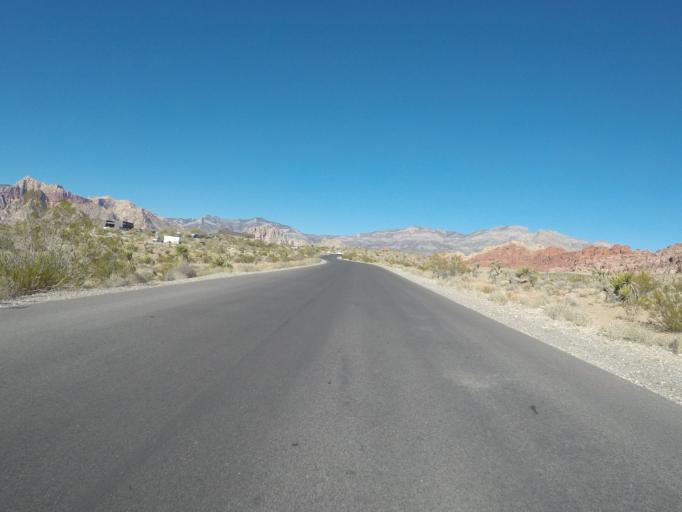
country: US
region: Nevada
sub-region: Clark County
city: Summerlin South
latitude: 36.1347
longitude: -115.4246
